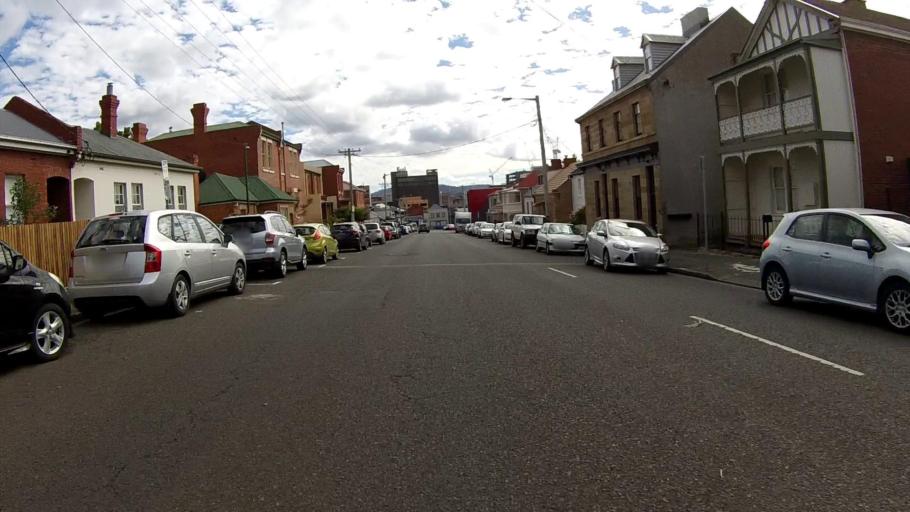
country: AU
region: Tasmania
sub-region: Hobart
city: Hobart
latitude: -42.8849
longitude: 147.3218
